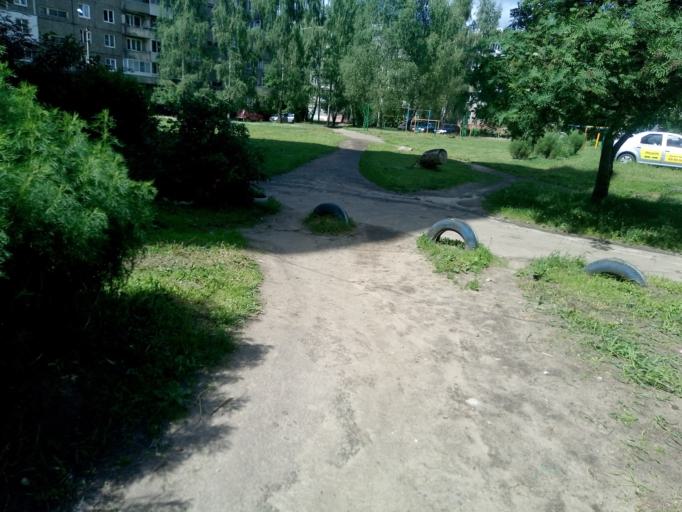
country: RU
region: Jaroslavl
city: Yaroslavl
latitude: 57.6559
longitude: 39.9582
